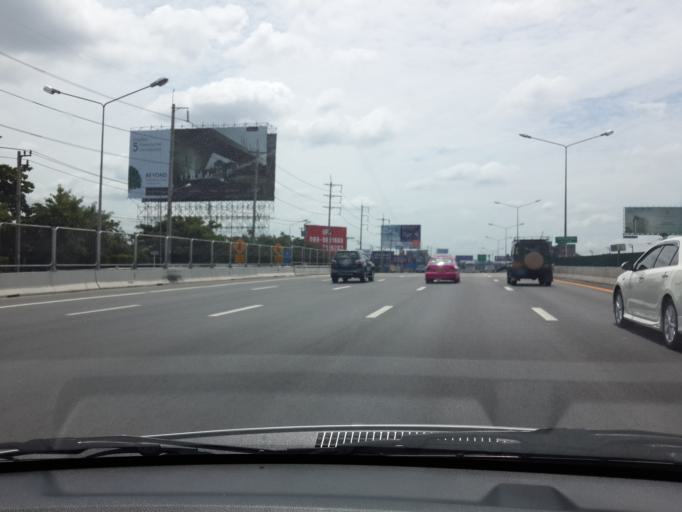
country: TH
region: Bangkok
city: Suan Luang
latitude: 13.7408
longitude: 100.6450
